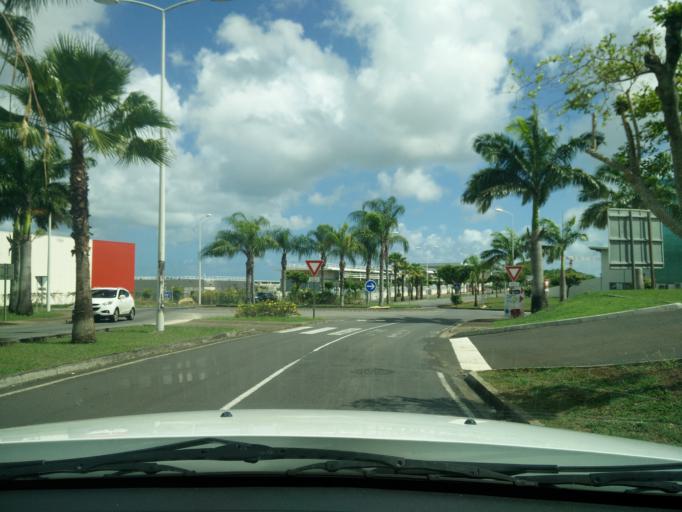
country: GP
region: Guadeloupe
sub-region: Guadeloupe
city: Les Abymes
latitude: 16.2673
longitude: -61.5176
